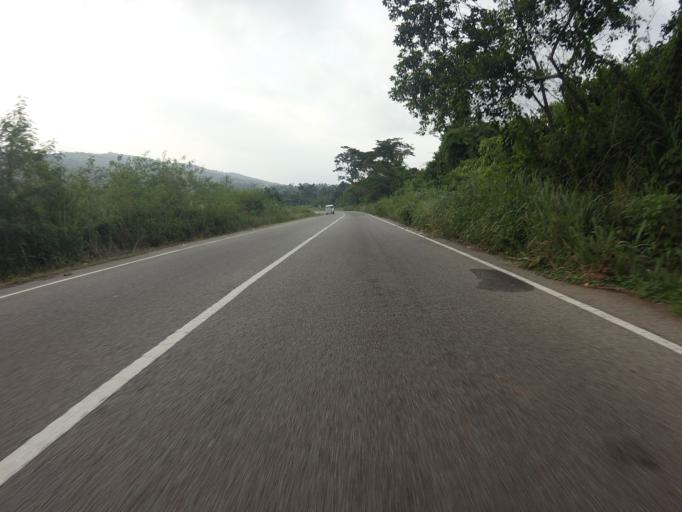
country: GH
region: Volta
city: Ho
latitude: 6.6465
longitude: 0.4699
